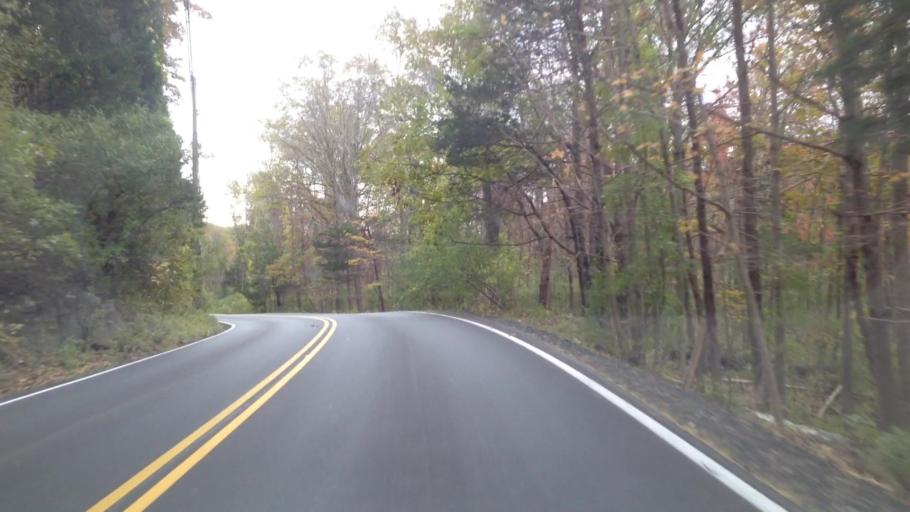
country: US
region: New York
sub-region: Ulster County
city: Tillson
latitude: 41.8227
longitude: -74.0355
